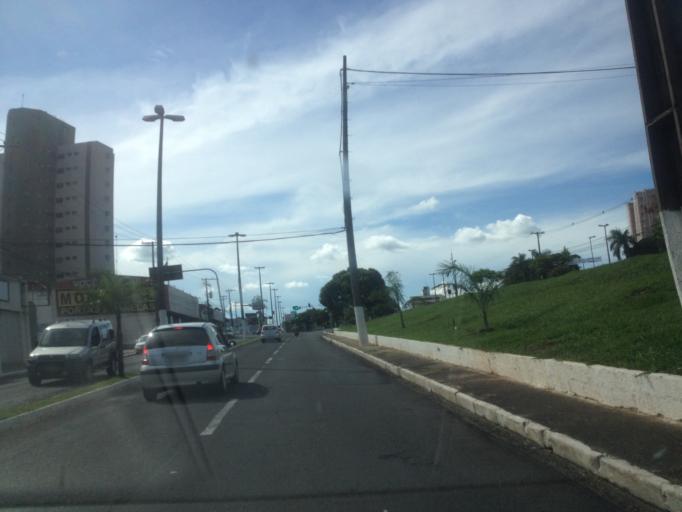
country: BR
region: Sao Paulo
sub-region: Marilia
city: Marilia
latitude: -22.2216
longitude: -49.9394
